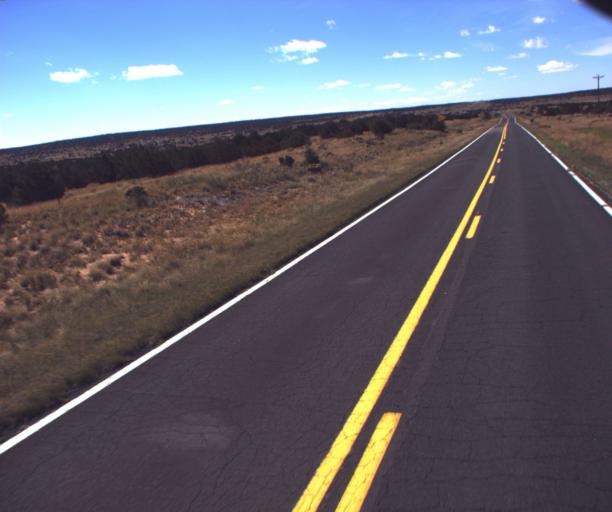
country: US
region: New Mexico
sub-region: McKinley County
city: Zuni Pueblo
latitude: 34.9871
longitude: -109.1183
